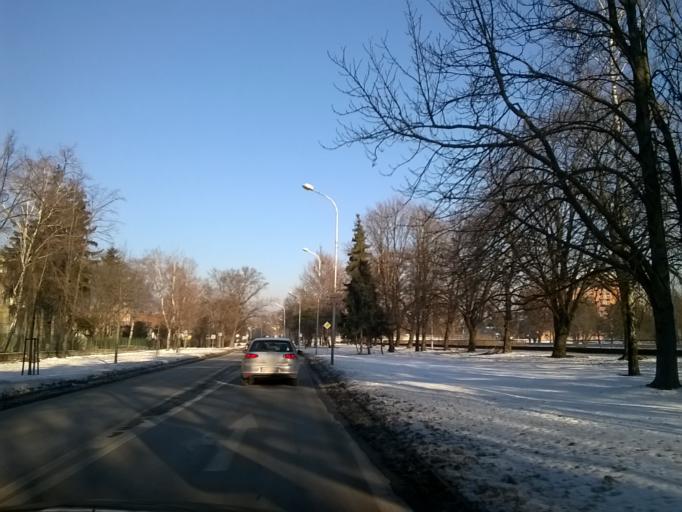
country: SK
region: Nitriansky
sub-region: Okres Nitra
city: Nitra
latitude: 48.3113
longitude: 18.0915
